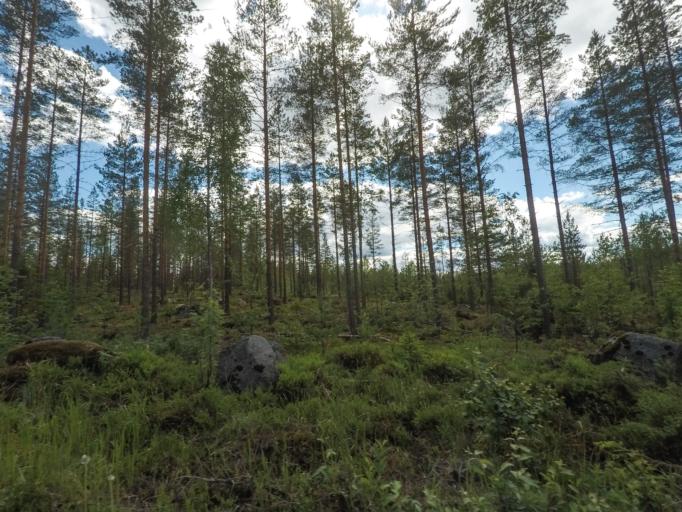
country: FI
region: Central Finland
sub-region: Jyvaeskylae
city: Hankasalmi
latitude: 62.4055
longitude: 26.6557
